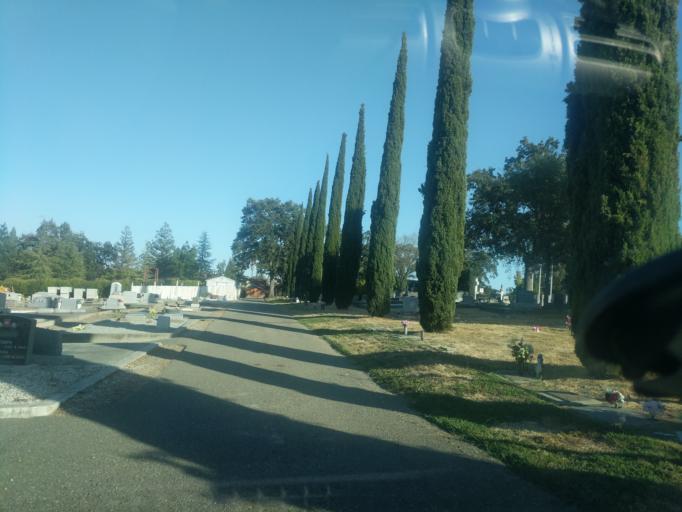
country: US
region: California
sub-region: Alameda County
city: Pleasanton
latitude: 37.6470
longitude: -121.8801
